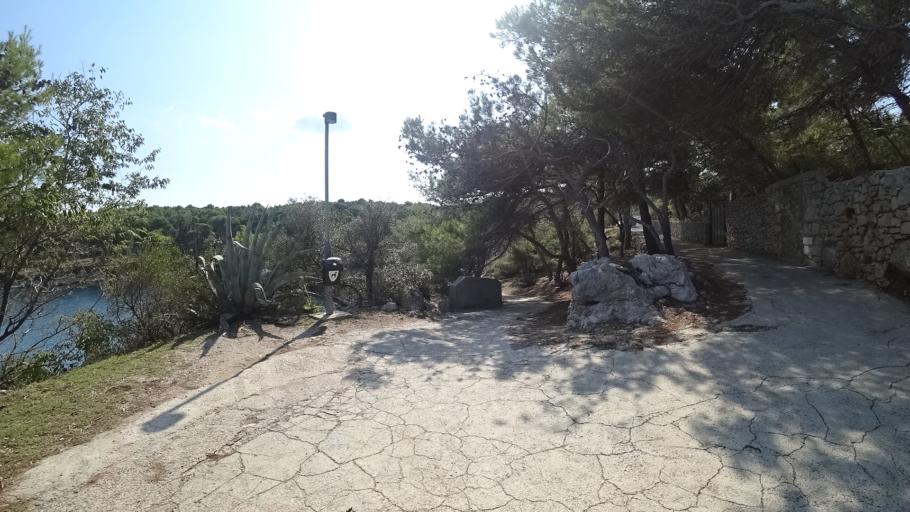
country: HR
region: Primorsko-Goranska
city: Mali Losinj
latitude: 44.5211
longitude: 14.5055
